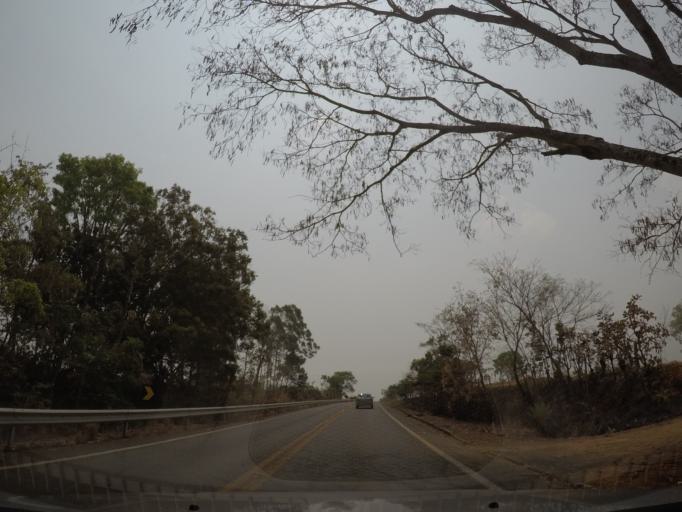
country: BR
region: Goias
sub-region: Pirenopolis
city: Pirenopolis
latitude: -15.8874
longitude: -48.8993
